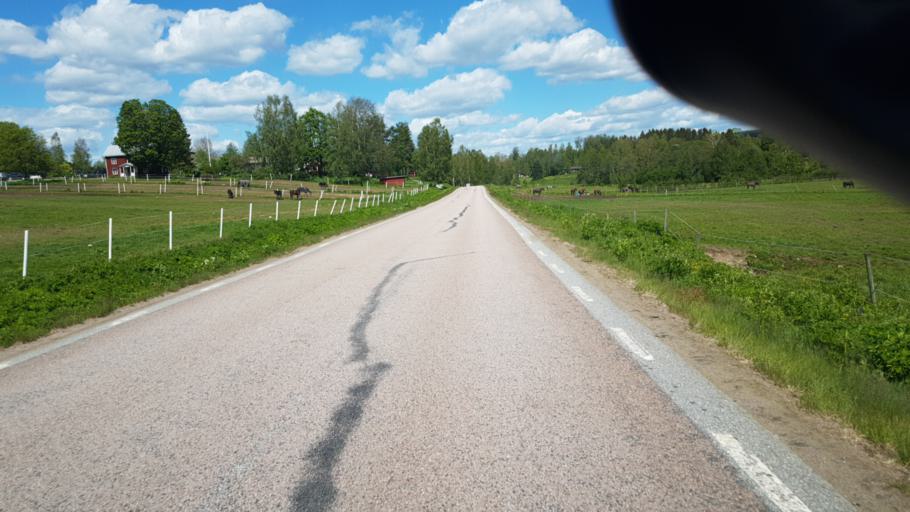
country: SE
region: Vaermland
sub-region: Arvika Kommun
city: Arvika
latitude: 59.7385
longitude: 12.8104
